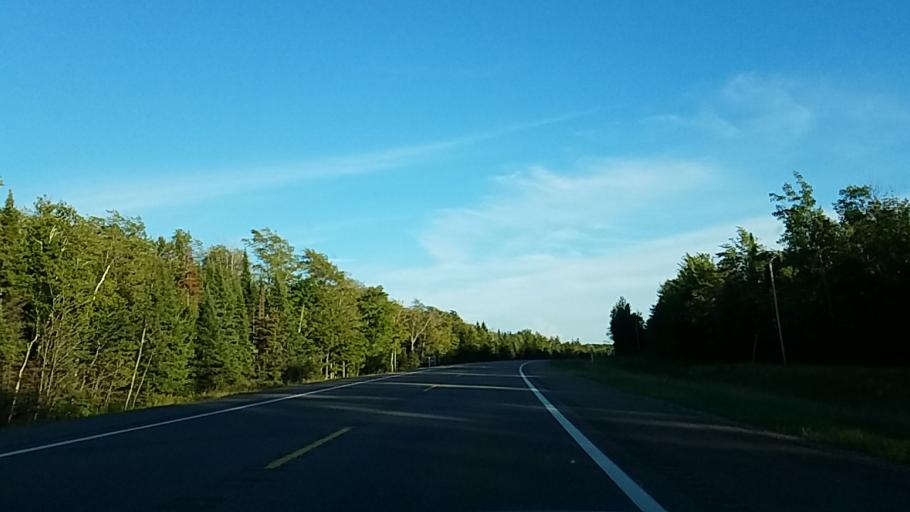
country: US
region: Michigan
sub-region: Alger County
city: Munising
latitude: 46.4595
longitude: -86.8939
